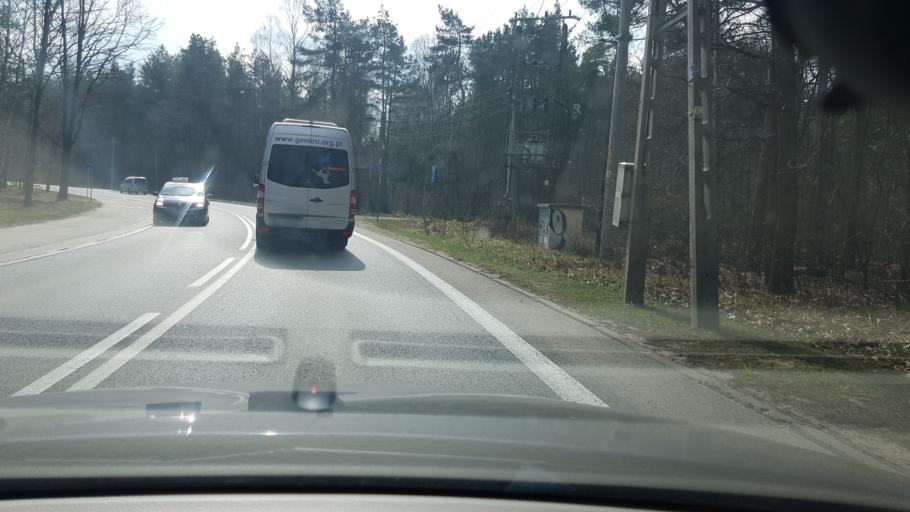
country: PL
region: Masovian Voivodeship
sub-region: Warszawa
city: Wesola
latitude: 52.2369
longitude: 21.2220
